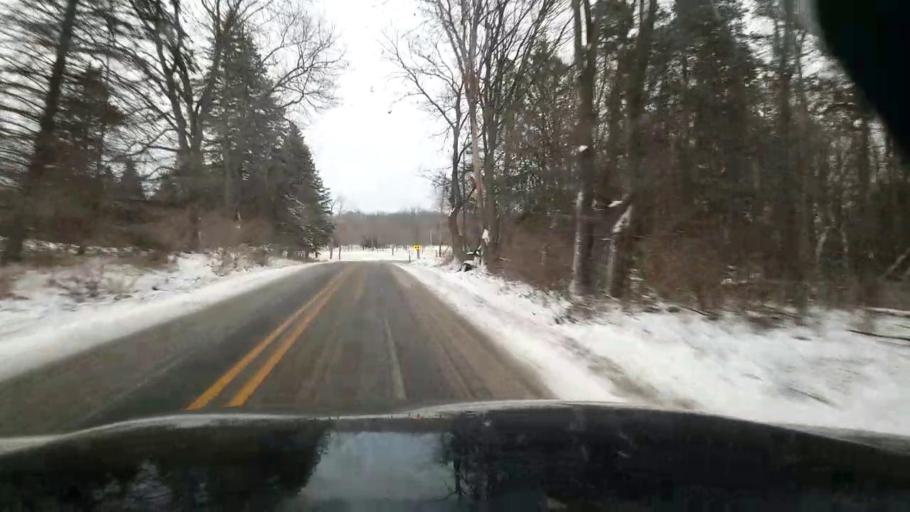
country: US
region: Michigan
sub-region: Jackson County
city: Vandercook Lake
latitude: 42.0947
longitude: -84.4672
